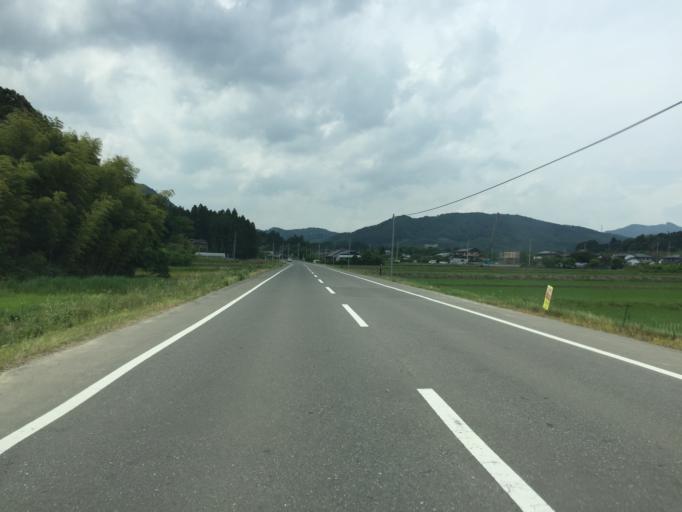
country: JP
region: Miyagi
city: Marumori
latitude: 37.8166
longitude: 140.8906
